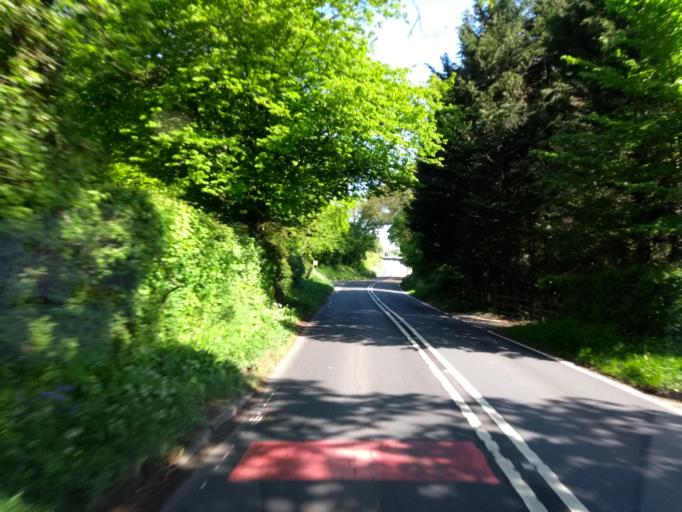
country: GB
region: England
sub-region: Devon
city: Axminster
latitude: 50.8045
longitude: -2.9799
